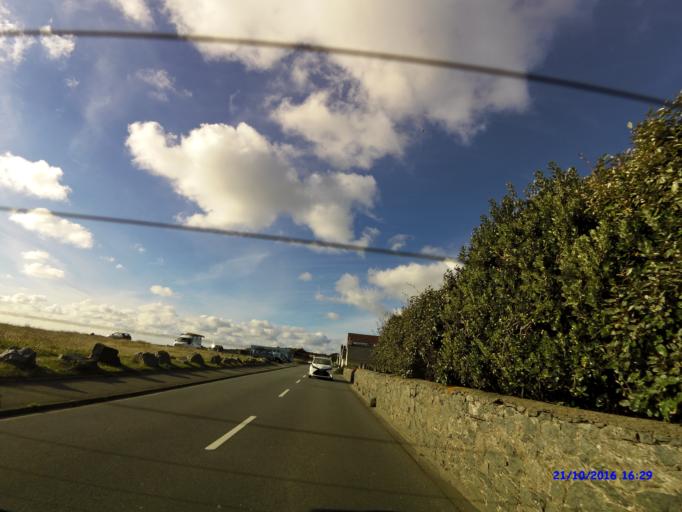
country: GG
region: St Peter Port
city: Saint Peter Port
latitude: 49.4538
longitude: -2.6506
